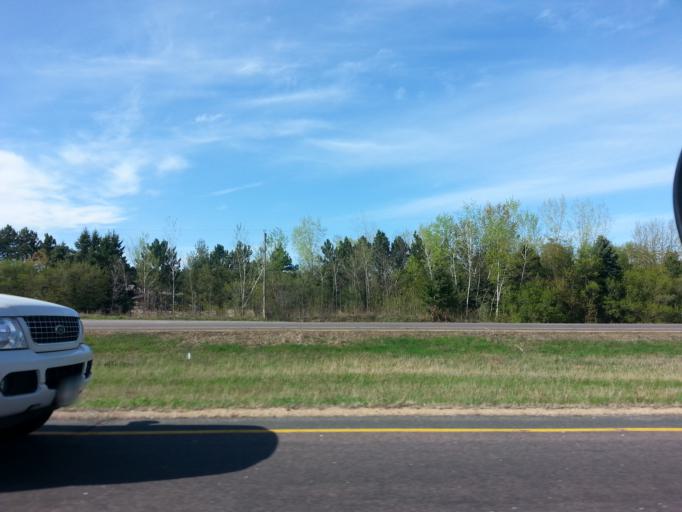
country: US
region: Minnesota
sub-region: Washington County
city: Lake Elmo
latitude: 45.0356
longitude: -92.8678
